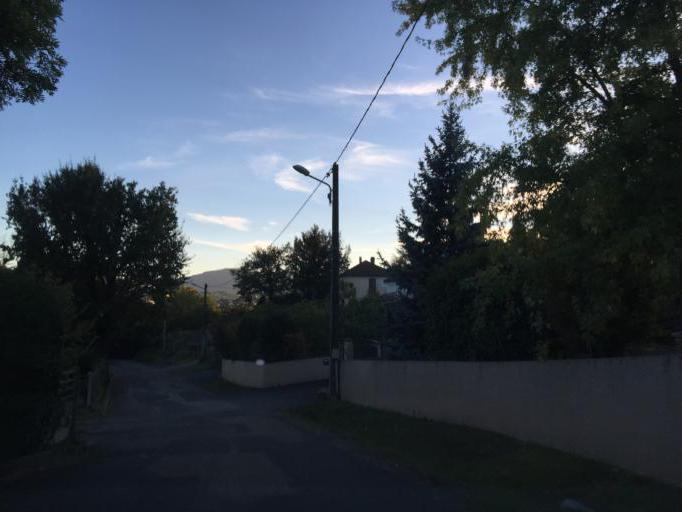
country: FR
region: Rhone-Alpes
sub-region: Departement de la Loire
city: Saint-Chamond
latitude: 45.4882
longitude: 4.5359
